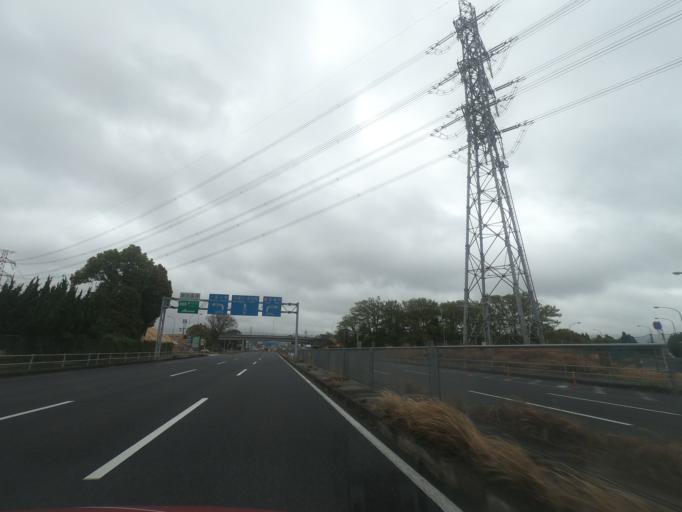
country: JP
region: Aichi
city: Kasugai
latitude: 35.2681
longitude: 136.9961
